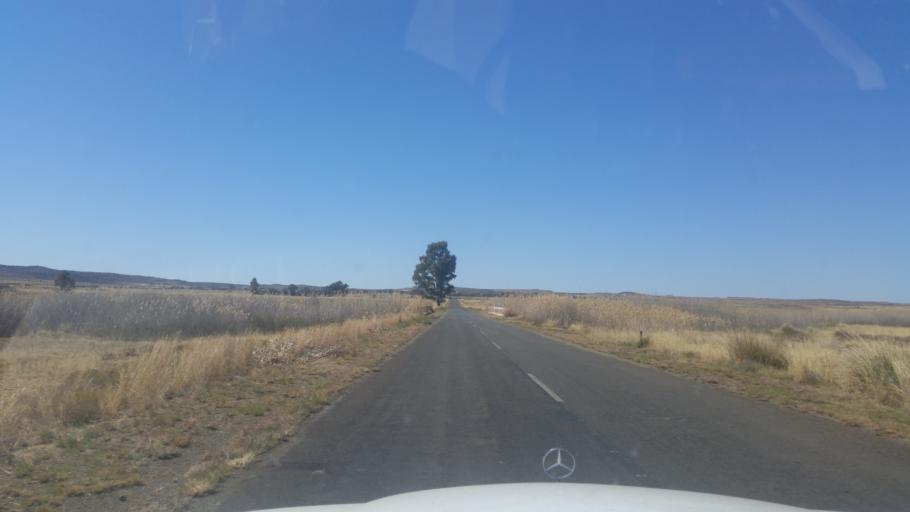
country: ZA
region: Eastern Cape
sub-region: Joe Gqabi District Municipality
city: Burgersdorp
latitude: -30.7571
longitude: 25.7766
